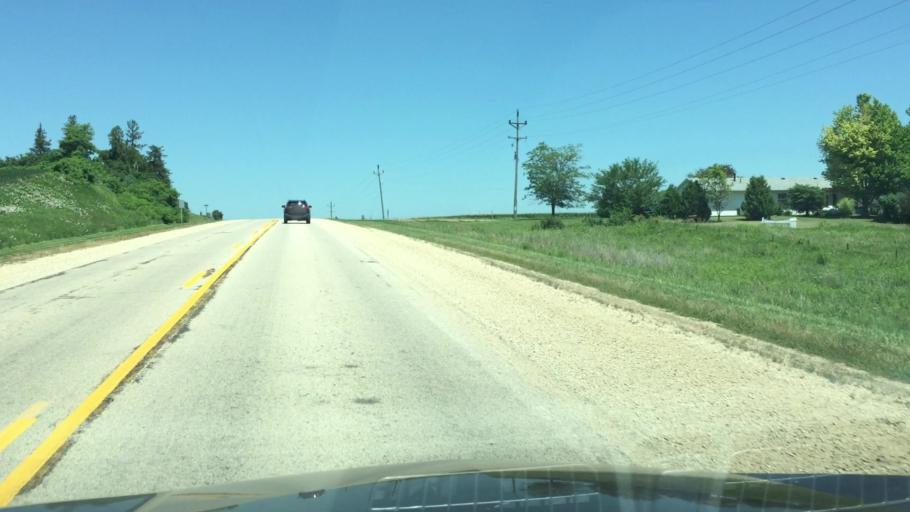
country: US
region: Iowa
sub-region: Cedar County
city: Mechanicsville
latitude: 41.9819
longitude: -91.1417
